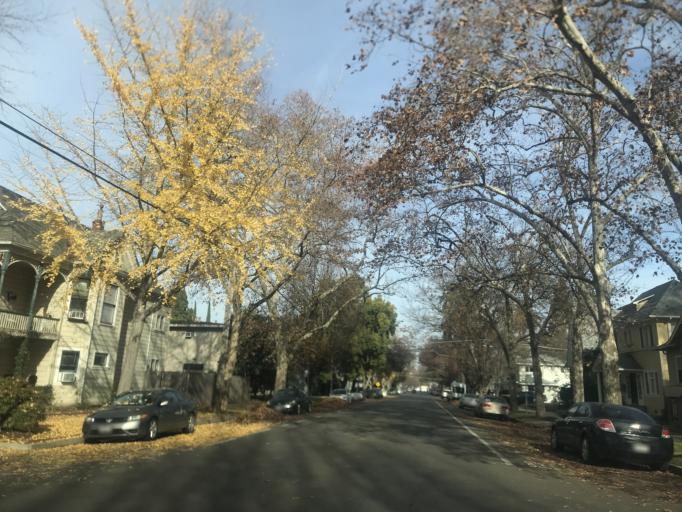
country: US
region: California
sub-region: Sacramento County
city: Sacramento
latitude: 38.5652
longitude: -121.4878
